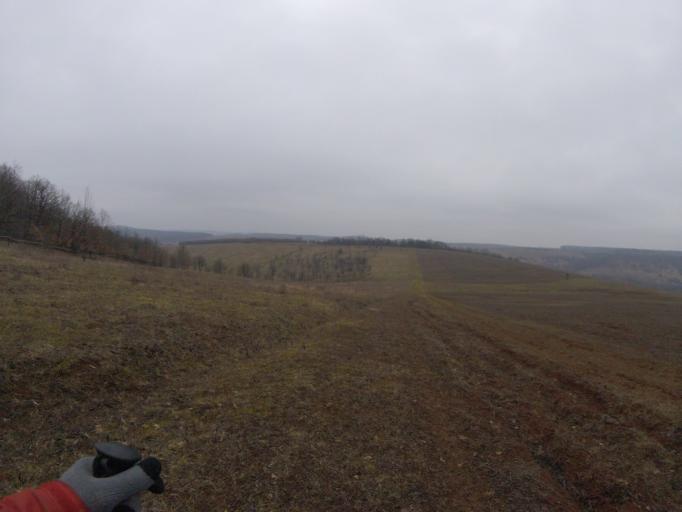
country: HU
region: Borsod-Abauj-Zemplen
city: Rudabanya
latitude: 48.4480
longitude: 20.5942
